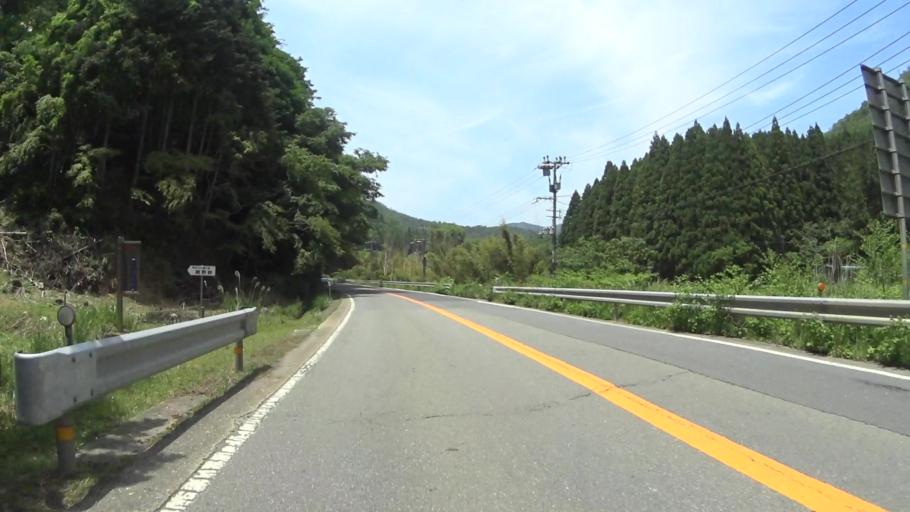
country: JP
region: Kyoto
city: Ayabe
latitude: 35.1956
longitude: 135.2857
